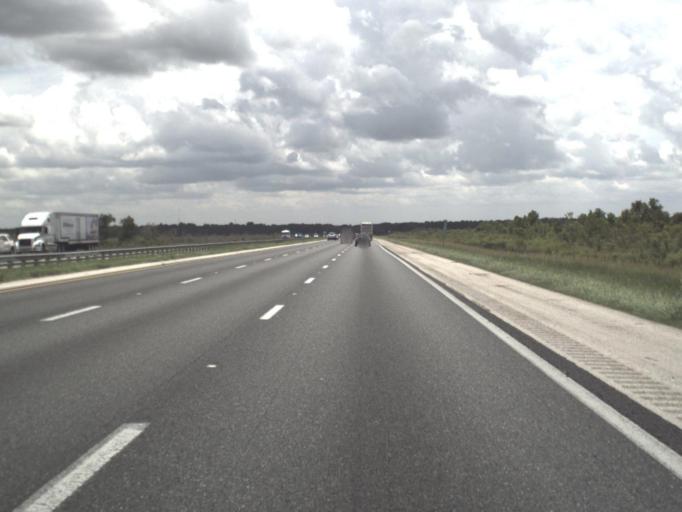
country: US
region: Florida
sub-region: Alachua County
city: Gainesville
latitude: 29.5721
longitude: -82.3524
